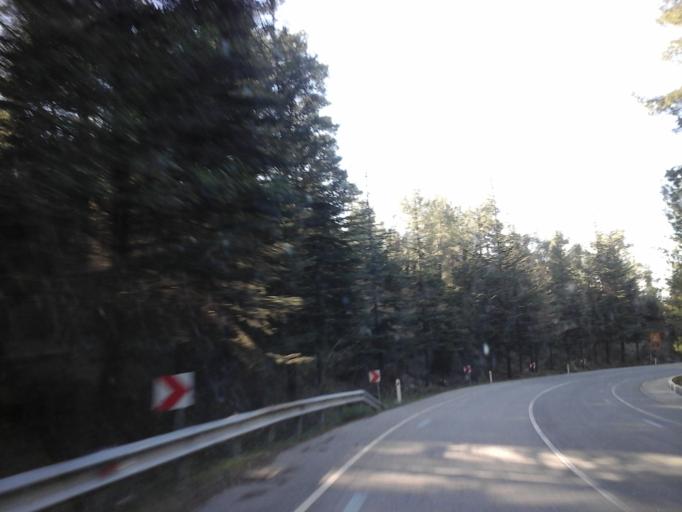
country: CY
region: Lefkosia
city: Kakopetria
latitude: 34.9506
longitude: 32.9259
